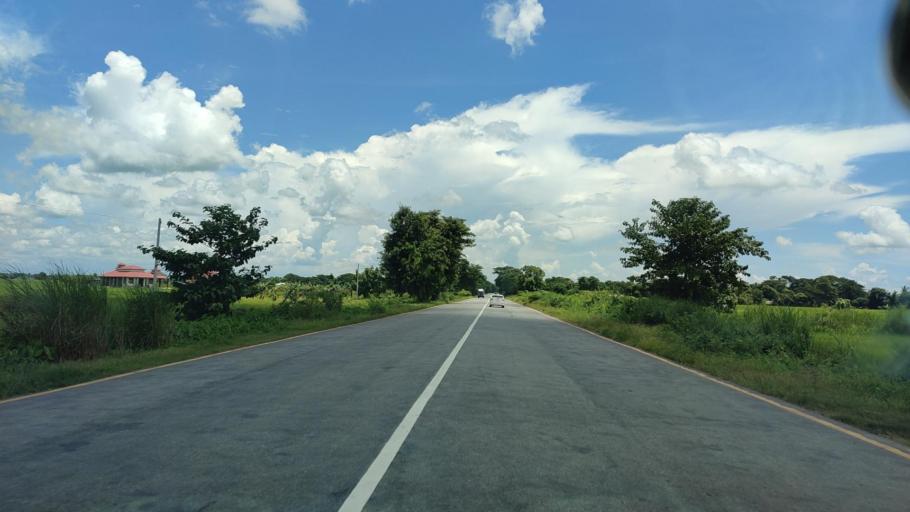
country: MM
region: Bago
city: Nyaunglebin
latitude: 18.1927
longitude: 96.5693
